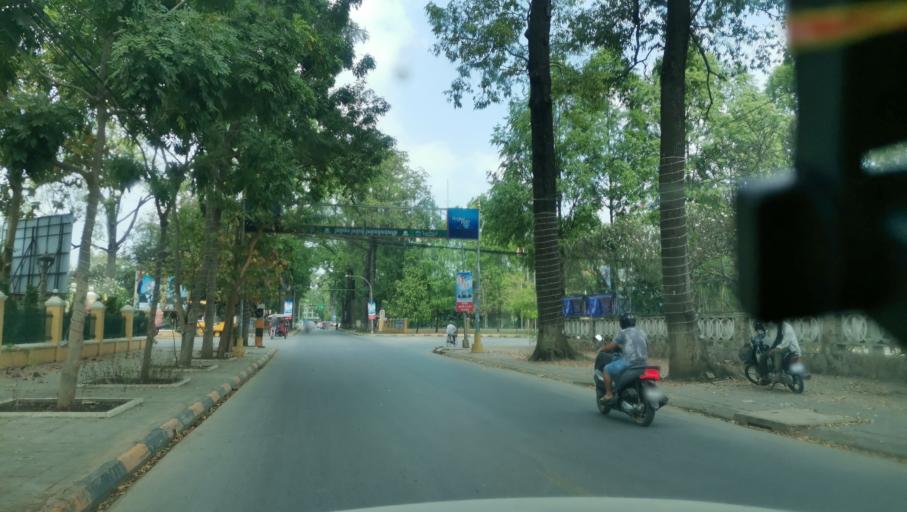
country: KH
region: Battambang
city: Battambang
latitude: 13.0899
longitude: 103.1997
